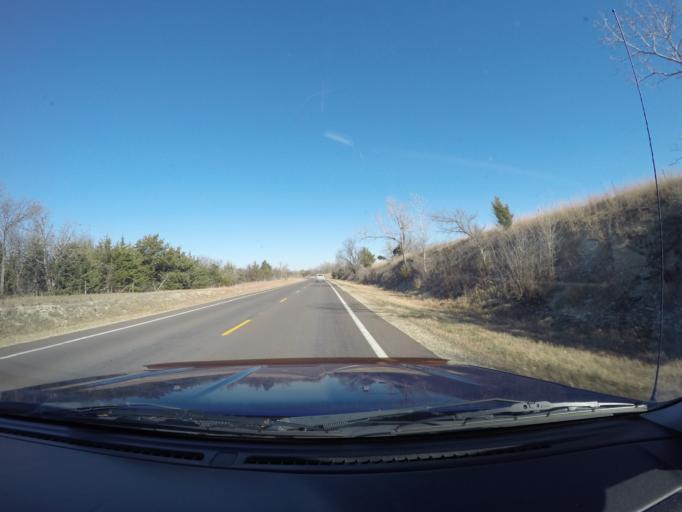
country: US
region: Kansas
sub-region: Marshall County
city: Blue Rapids
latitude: 39.4976
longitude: -96.7545
